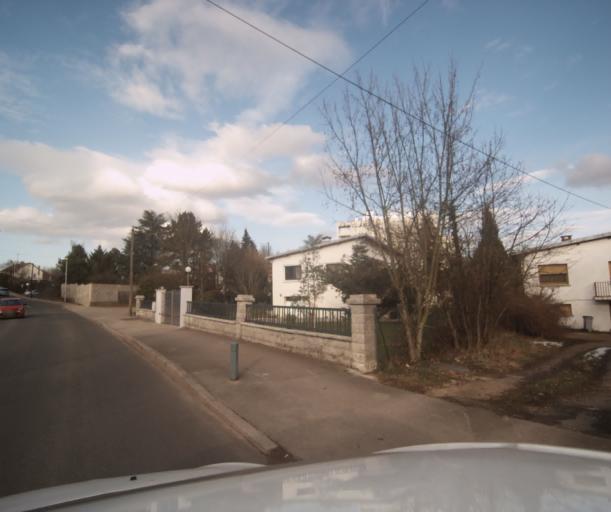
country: FR
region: Franche-Comte
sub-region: Departement du Doubs
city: Besancon
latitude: 47.2580
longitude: 6.0286
